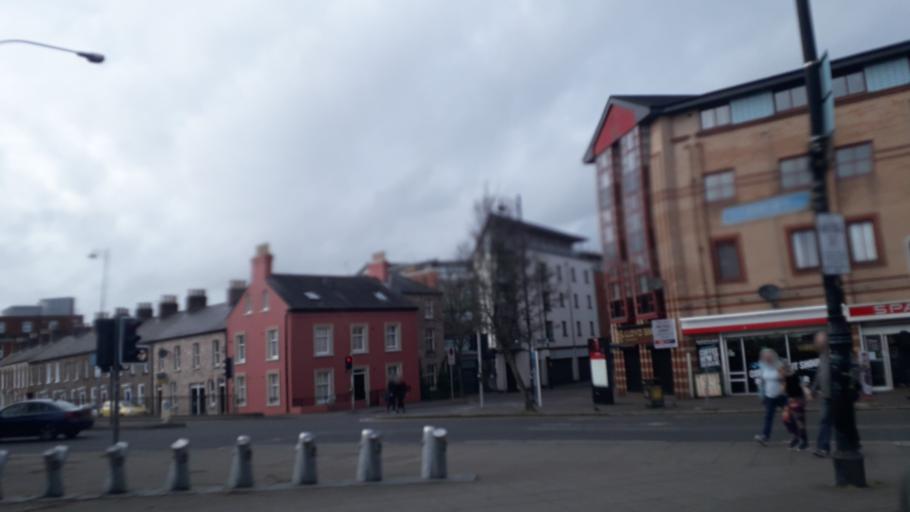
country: GB
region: Northern Ireland
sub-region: City of Belfast
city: Belfast
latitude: 54.5881
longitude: -5.9355
